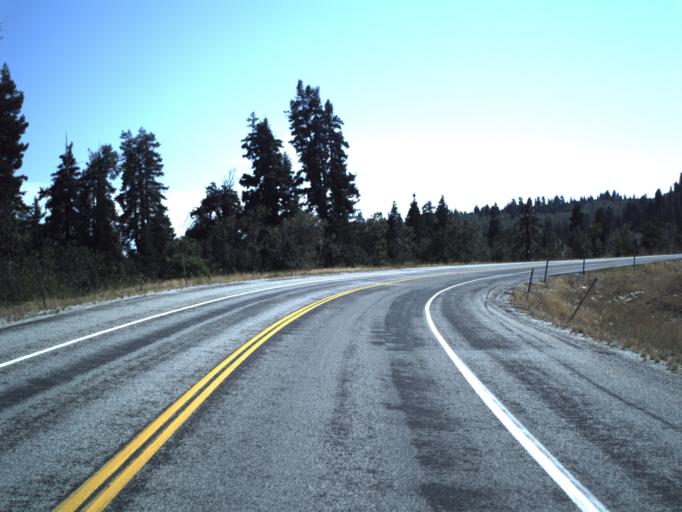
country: US
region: Utah
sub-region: Morgan County
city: Mountain Green
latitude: 41.2175
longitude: -111.8514
